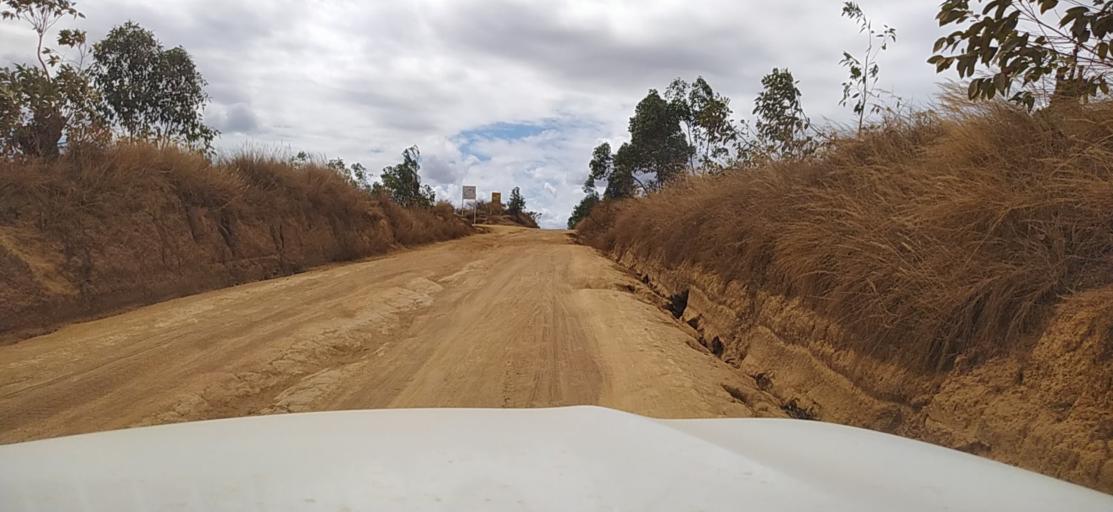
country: MG
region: Alaotra Mangoro
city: Ambatondrazaka
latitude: -17.9484
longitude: 48.2488
